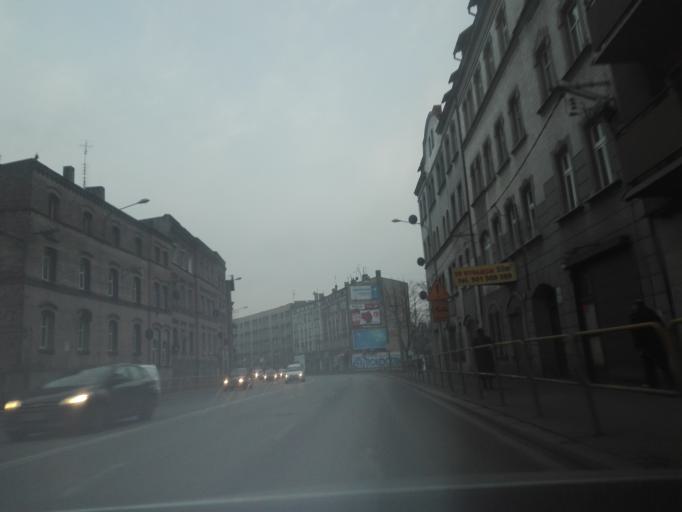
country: PL
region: Silesian Voivodeship
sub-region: Chorzow
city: Chorzow
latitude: 50.2936
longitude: 18.9573
